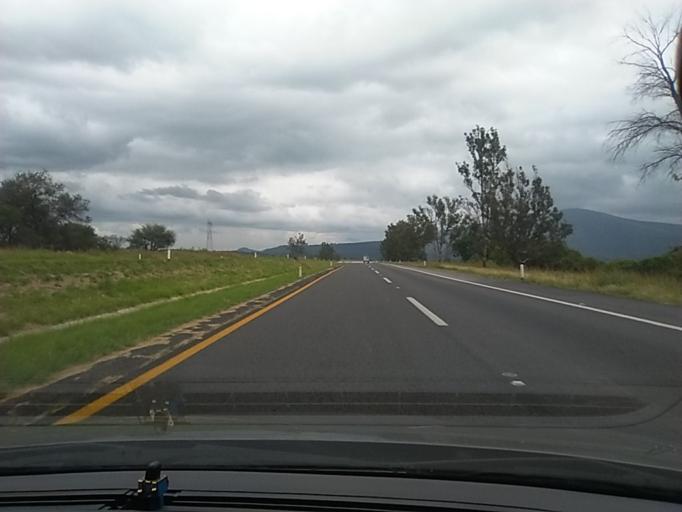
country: MX
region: Jalisco
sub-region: Zapotlanejo
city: La Mezquitera
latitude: 20.5684
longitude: -103.0807
